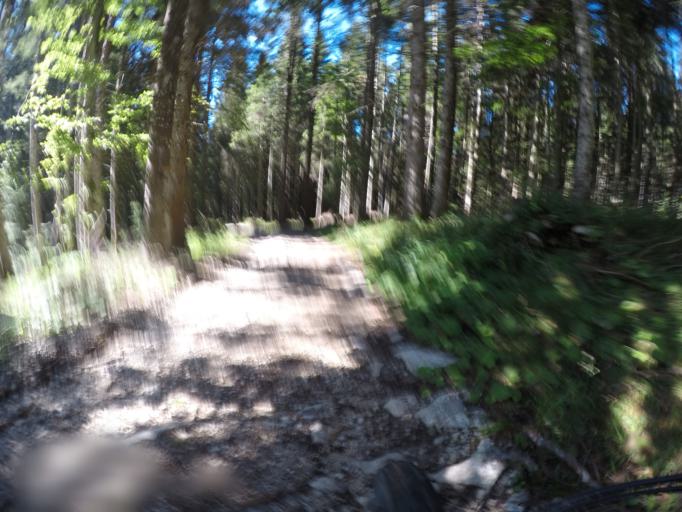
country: IT
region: Veneto
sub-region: Provincia di Vicenza
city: Asiago
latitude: 45.9094
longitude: 11.4841
